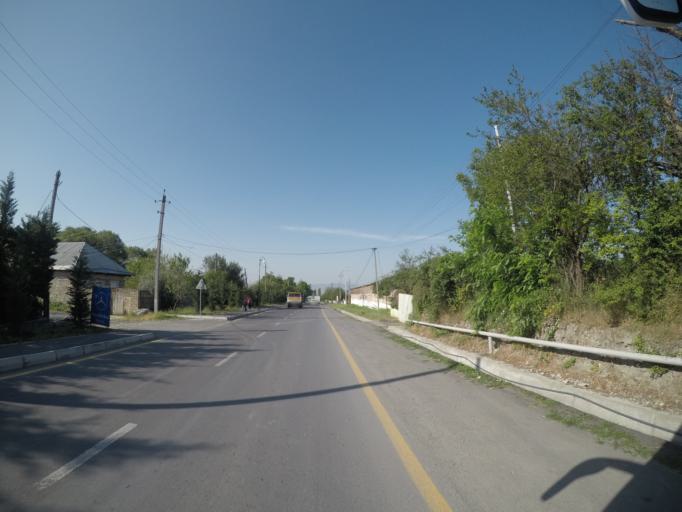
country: AZ
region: Shaki City
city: Sheki
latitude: 41.2156
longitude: 47.1683
